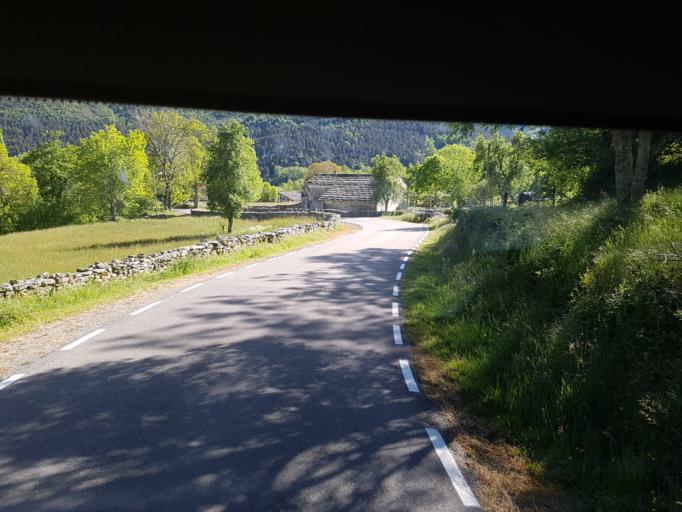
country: ES
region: Castille and Leon
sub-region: Provincia de Burgos
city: Espinosa de los Monteros
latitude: 43.1200
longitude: -3.5800
